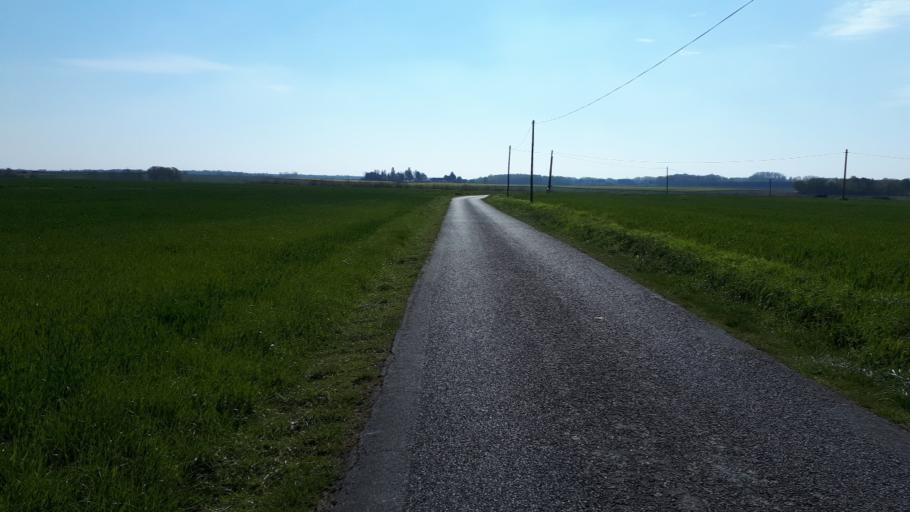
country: FR
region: Centre
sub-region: Departement du Loir-et-Cher
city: Saint-Romain-sur-Cher
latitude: 47.3760
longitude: 1.3856
